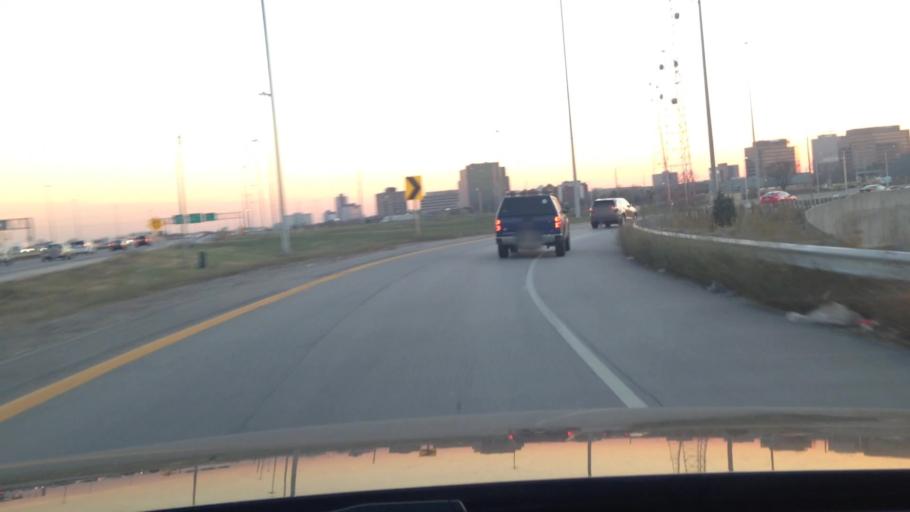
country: US
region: Illinois
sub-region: Cook County
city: Rolling Meadows
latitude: 42.0605
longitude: -88.0288
